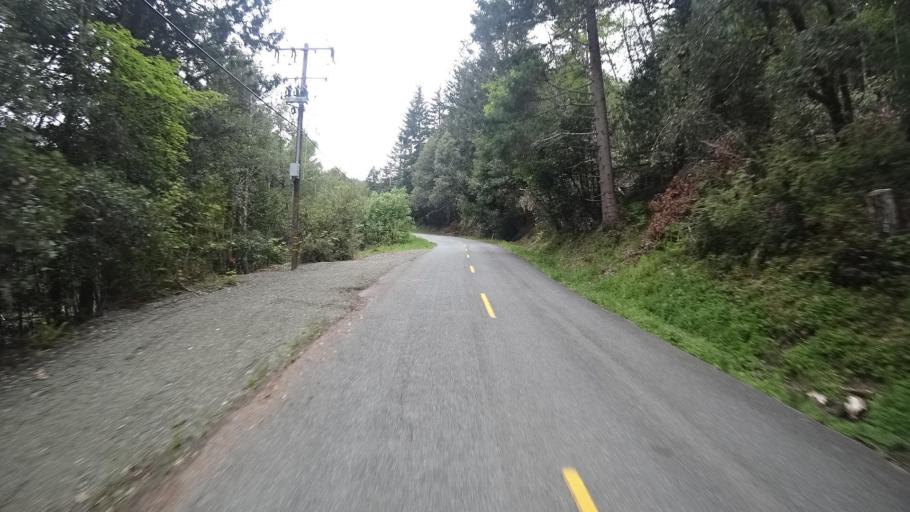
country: US
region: California
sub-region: Humboldt County
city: Blue Lake
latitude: 40.9381
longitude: -123.8460
